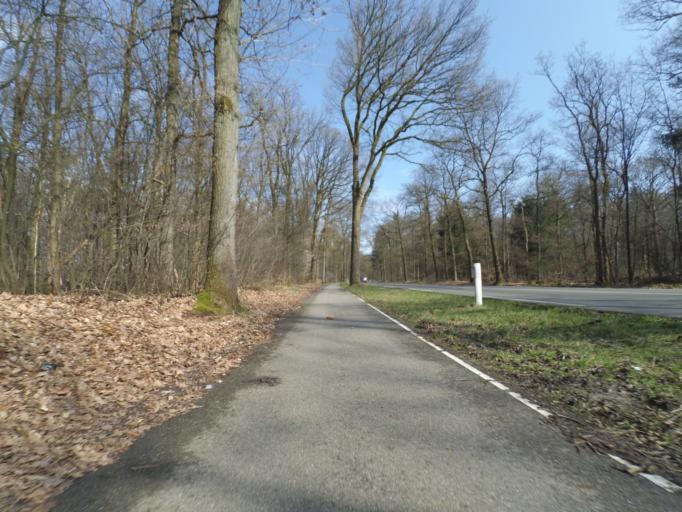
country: NL
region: Gelderland
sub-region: Gemeente Apeldoorn
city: Beekbergen
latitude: 52.1304
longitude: 5.8799
